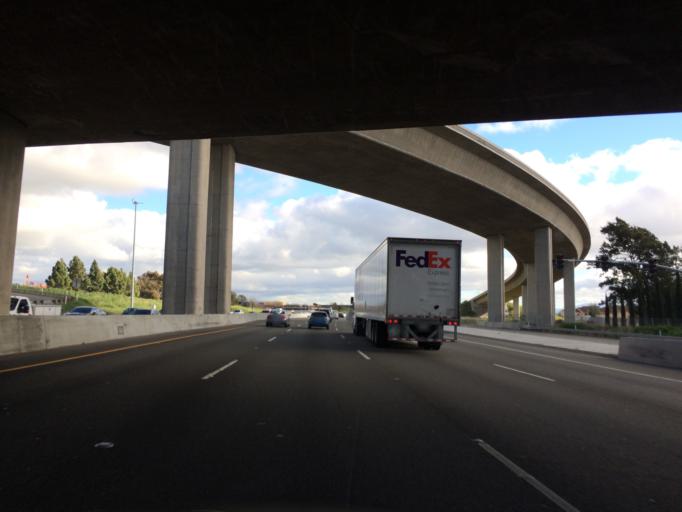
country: US
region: California
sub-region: Santa Clara County
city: Milpitas
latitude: 37.4839
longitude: -121.9373
